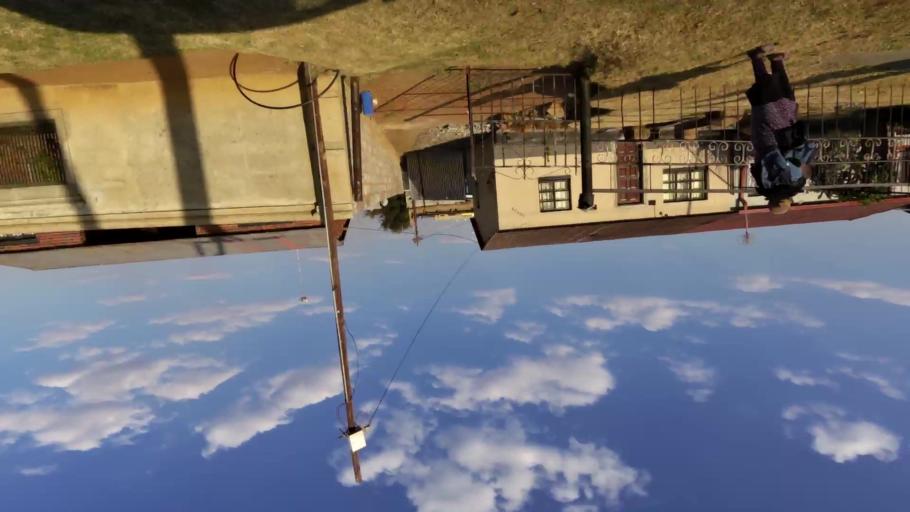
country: ZA
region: Gauteng
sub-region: City of Johannesburg Metropolitan Municipality
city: Soweto
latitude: -26.2256
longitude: 27.9061
